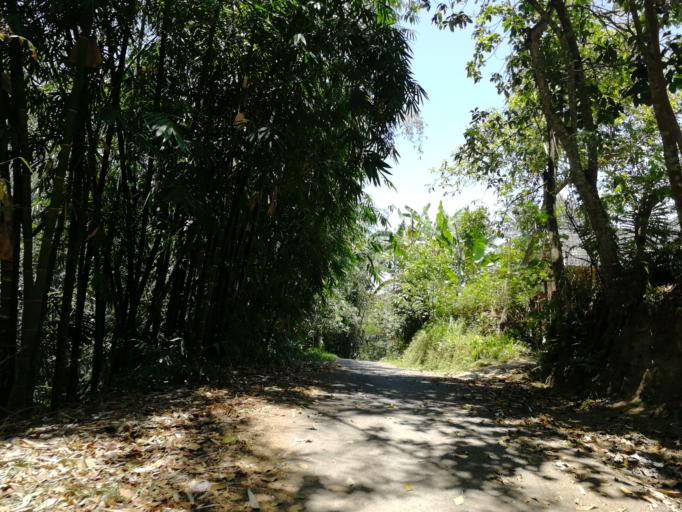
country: ID
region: West Nusa Tenggara
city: Tetebatu
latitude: -8.5459
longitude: 116.4202
